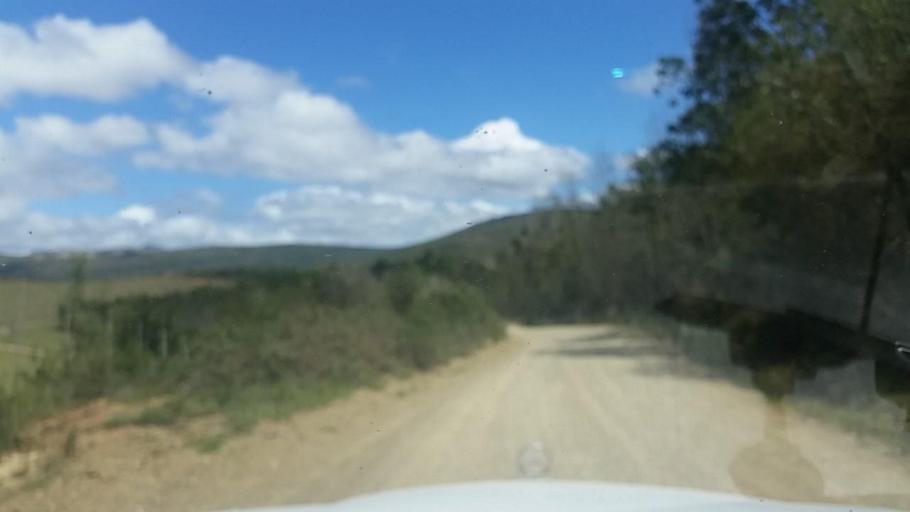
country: ZA
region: Western Cape
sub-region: Eden District Municipality
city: Knysna
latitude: -33.8573
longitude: 23.1882
